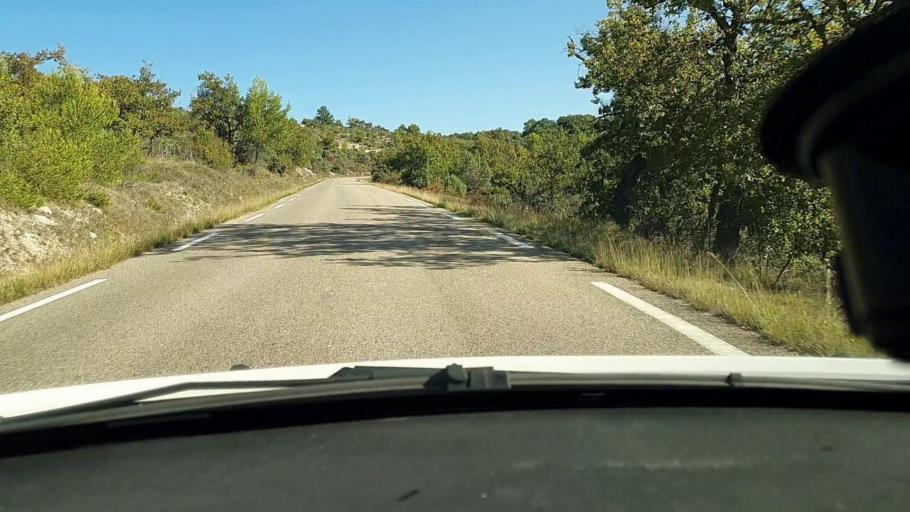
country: FR
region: Languedoc-Roussillon
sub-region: Departement du Gard
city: Goudargues
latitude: 44.2813
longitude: 4.4565
